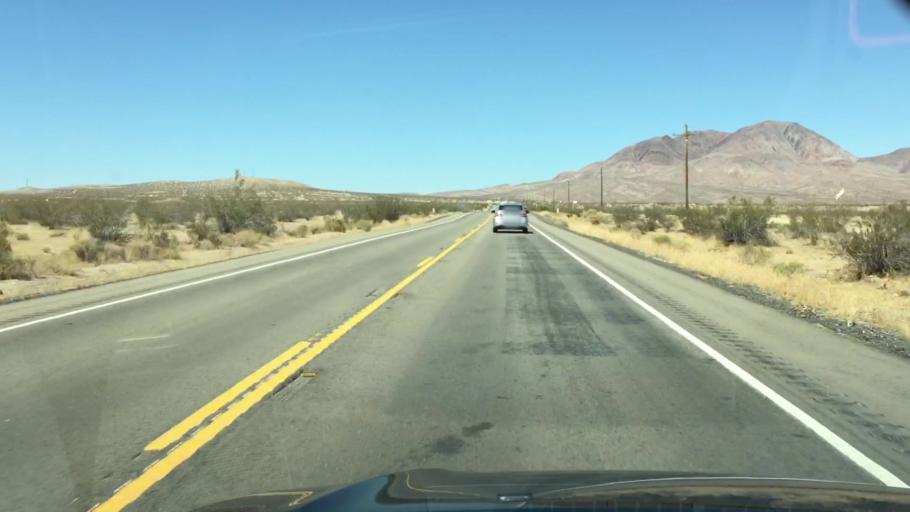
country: US
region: California
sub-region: Kern County
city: Boron
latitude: 35.2950
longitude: -117.6146
